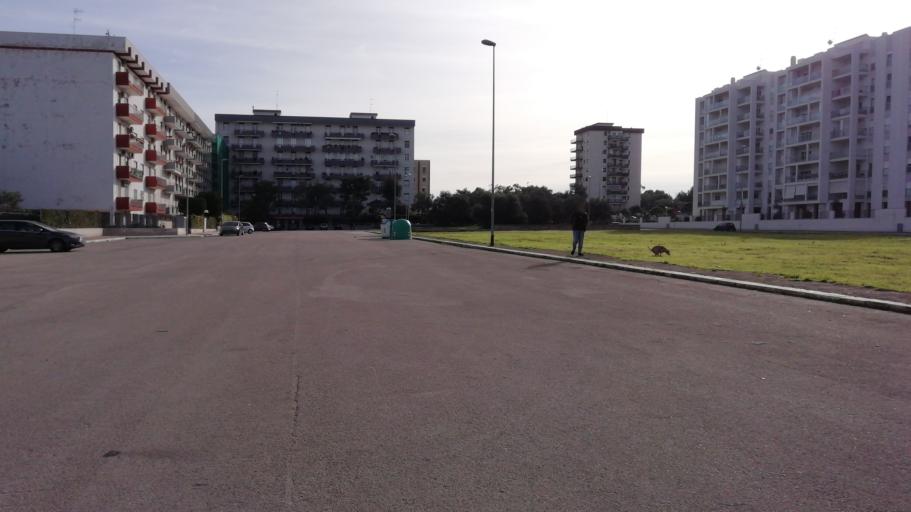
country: IT
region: Apulia
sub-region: Provincia di Bari
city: Triggiano
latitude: 41.1036
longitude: 16.9149
